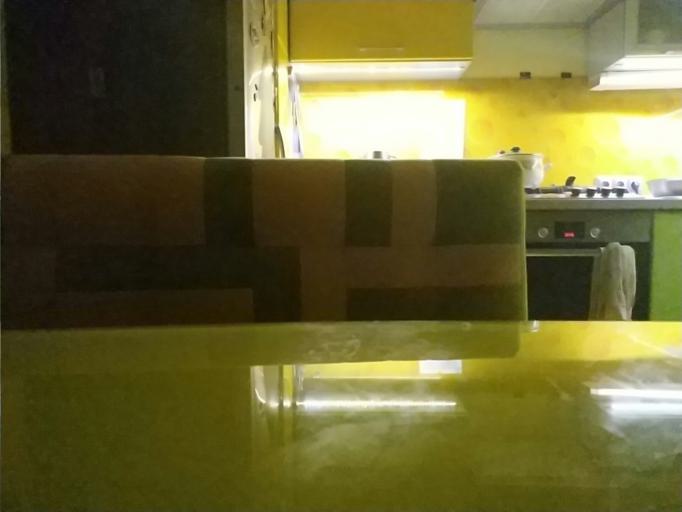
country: RU
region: Republic of Karelia
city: Kalevala
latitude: 65.2131
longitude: 30.7412
